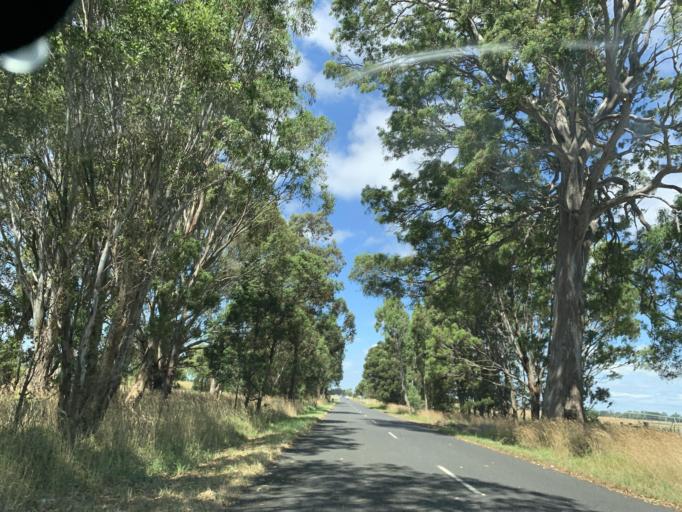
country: AU
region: Victoria
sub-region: Wellington
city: Heyfield
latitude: -38.0102
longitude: 146.6585
